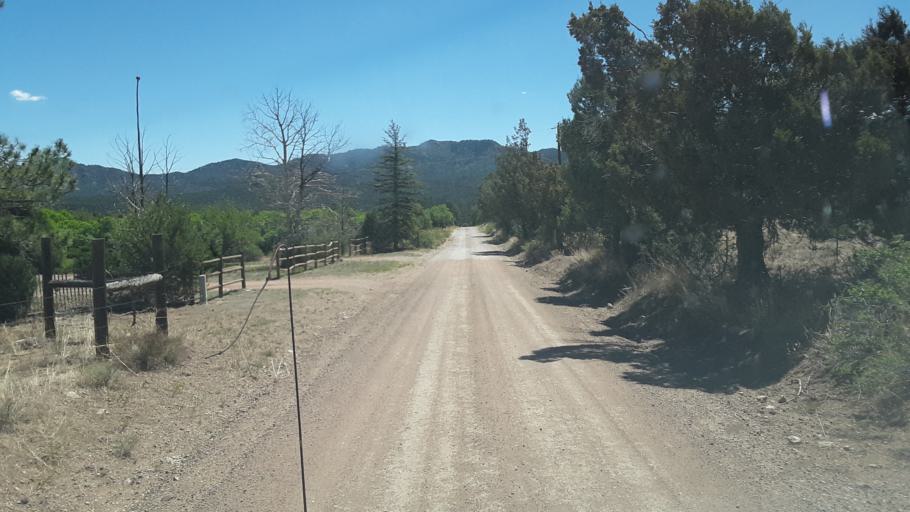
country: US
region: Colorado
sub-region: Custer County
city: Westcliffe
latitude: 38.2836
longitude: -105.6103
